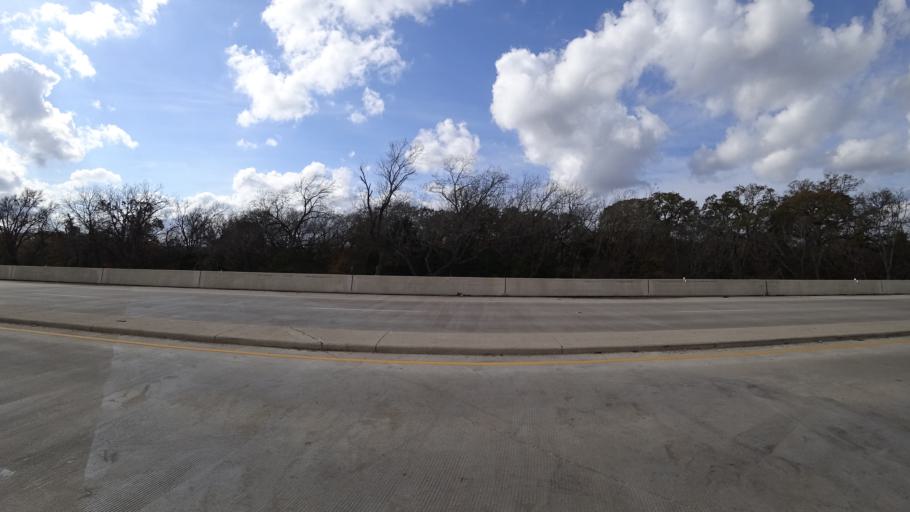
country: US
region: Texas
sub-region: Williamson County
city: Brushy Creek
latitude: 30.4842
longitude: -97.7202
